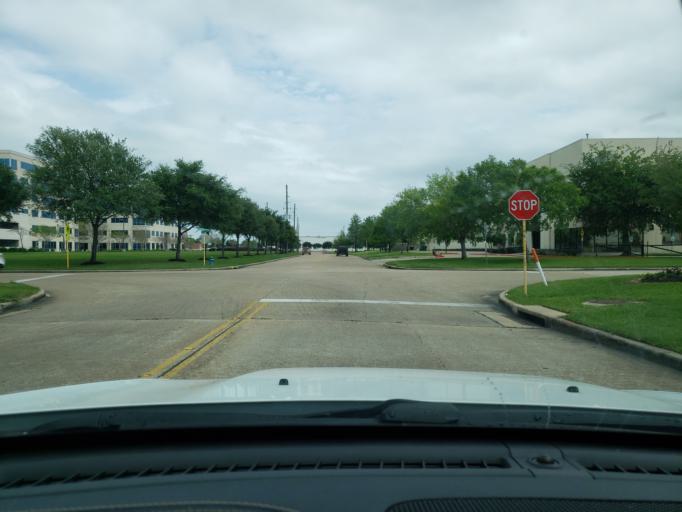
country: US
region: Texas
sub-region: Harris County
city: Jersey Village
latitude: 29.9189
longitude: -95.5596
